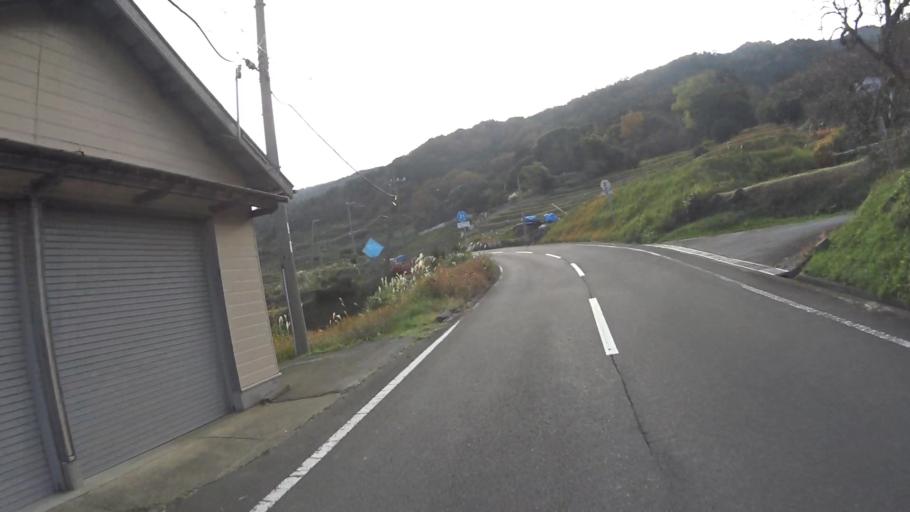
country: JP
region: Kyoto
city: Maizuru
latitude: 35.5543
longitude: 135.3959
